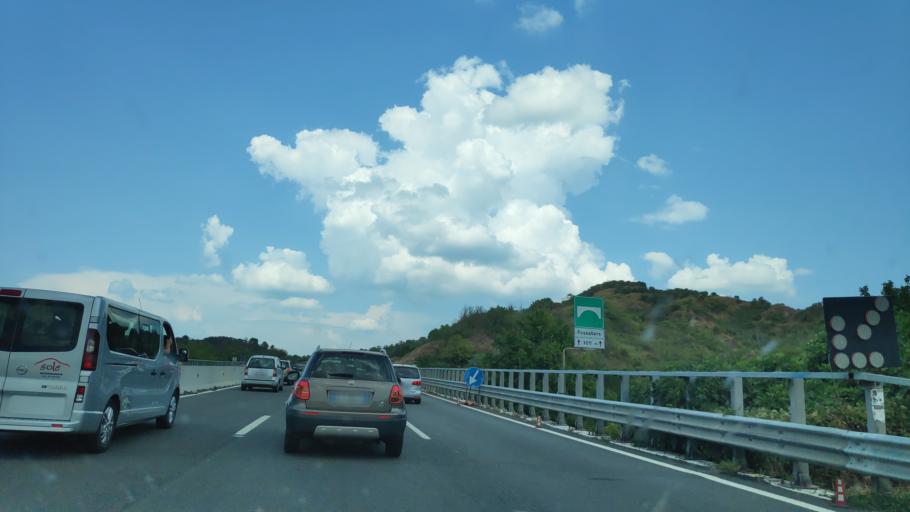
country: IT
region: Umbria
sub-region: Provincia di Terni
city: Ficulle
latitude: 42.8310
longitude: 12.0427
